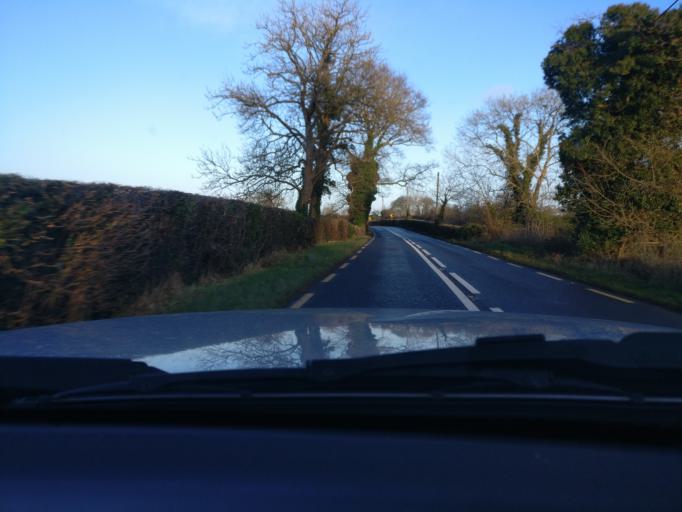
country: IE
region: Ulster
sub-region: An Cabhan
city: Kingscourt
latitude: 53.7938
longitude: -6.7193
